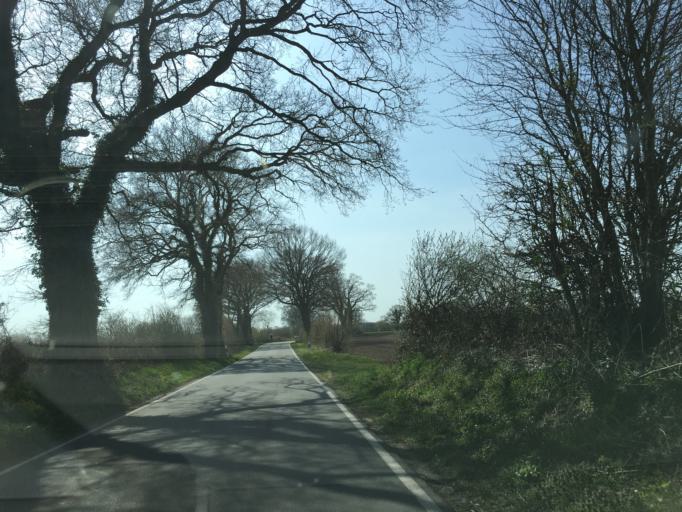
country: DE
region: Schleswig-Holstein
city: Felm
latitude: 54.4028
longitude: 10.0564
